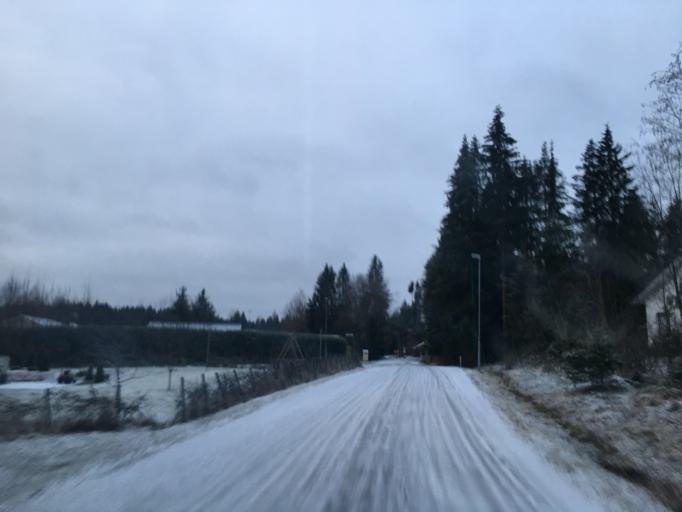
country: FI
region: Varsinais-Suomi
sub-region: Loimaa
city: Aura
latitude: 60.6489
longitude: 22.5696
